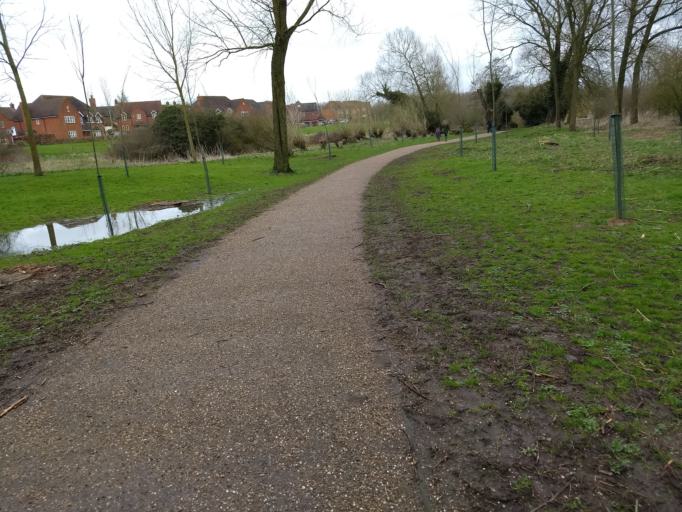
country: GB
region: England
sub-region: Milton Keynes
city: Stony Stratford
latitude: 52.0621
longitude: -0.8604
